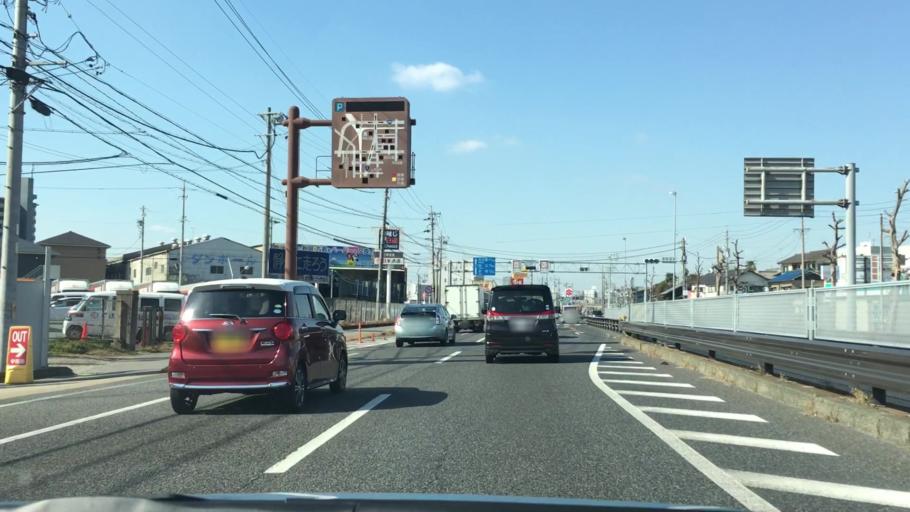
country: JP
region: Aichi
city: Okazaki
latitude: 34.9479
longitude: 137.1854
